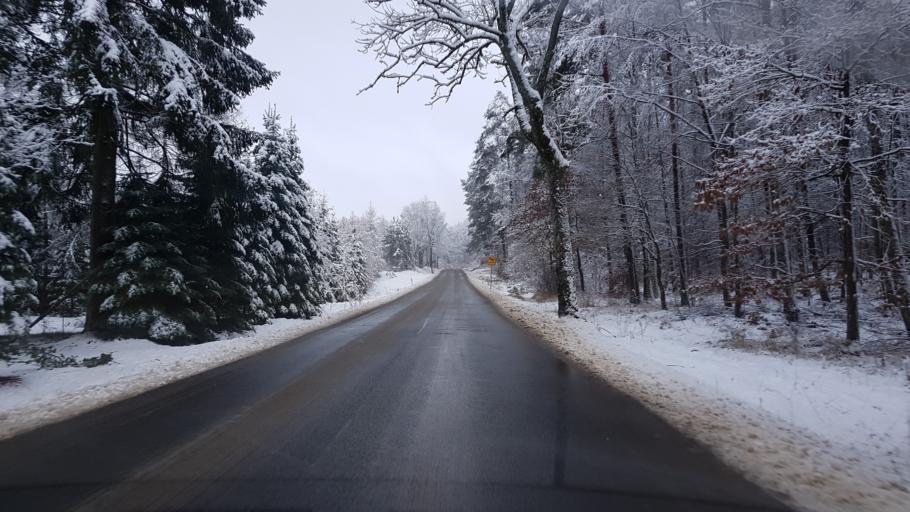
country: PL
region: West Pomeranian Voivodeship
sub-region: Powiat drawski
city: Zlocieniec
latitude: 53.5956
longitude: 16.0039
